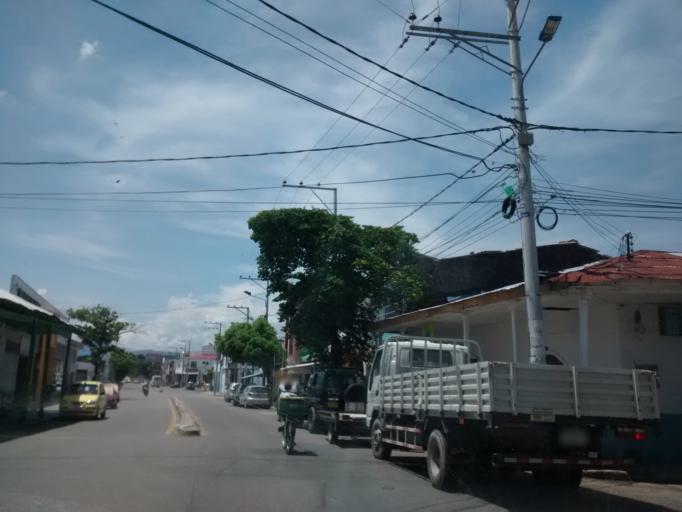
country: CO
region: Cundinamarca
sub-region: Girardot
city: Girardot City
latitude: 4.2989
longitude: -74.8029
